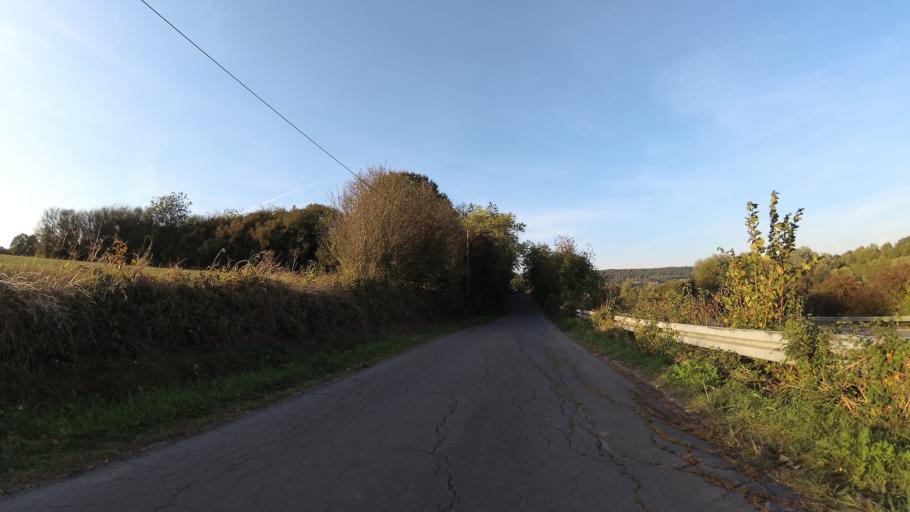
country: DE
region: Saarland
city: Ottweiler
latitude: 49.4226
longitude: 7.1613
